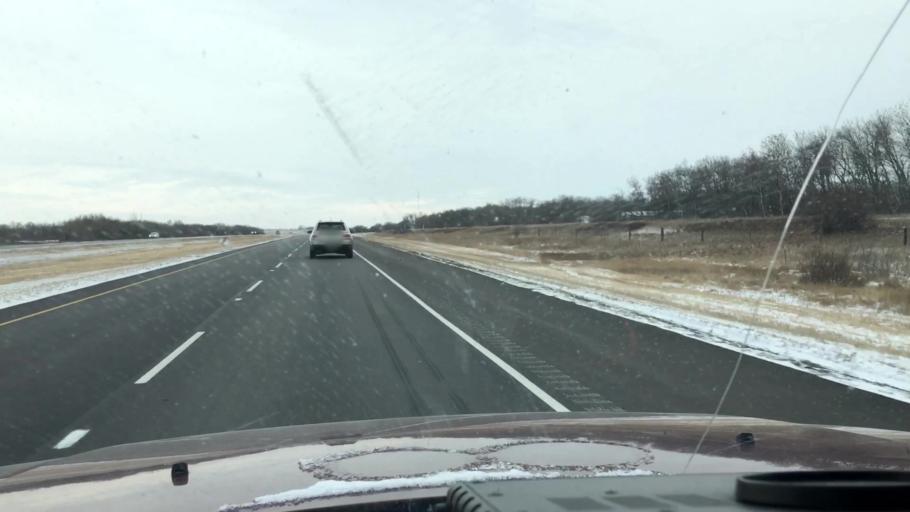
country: CA
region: Saskatchewan
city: Saskatoon
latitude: 51.8782
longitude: -106.5113
